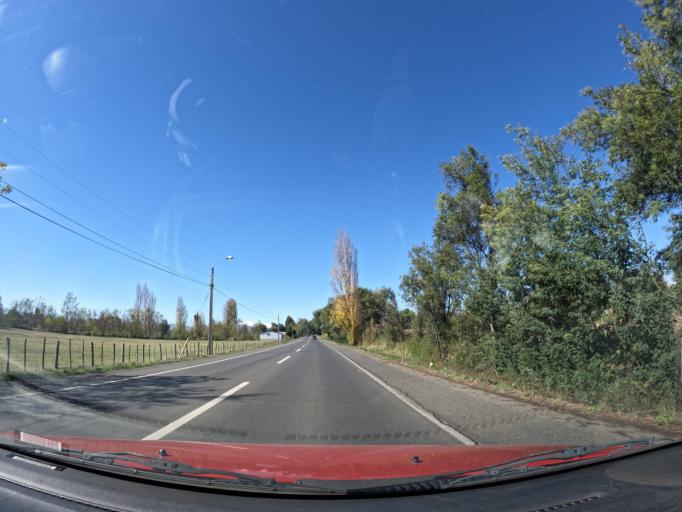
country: CL
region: Biobio
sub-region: Provincia de Nuble
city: Coihueco
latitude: -36.6876
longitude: -71.9099
